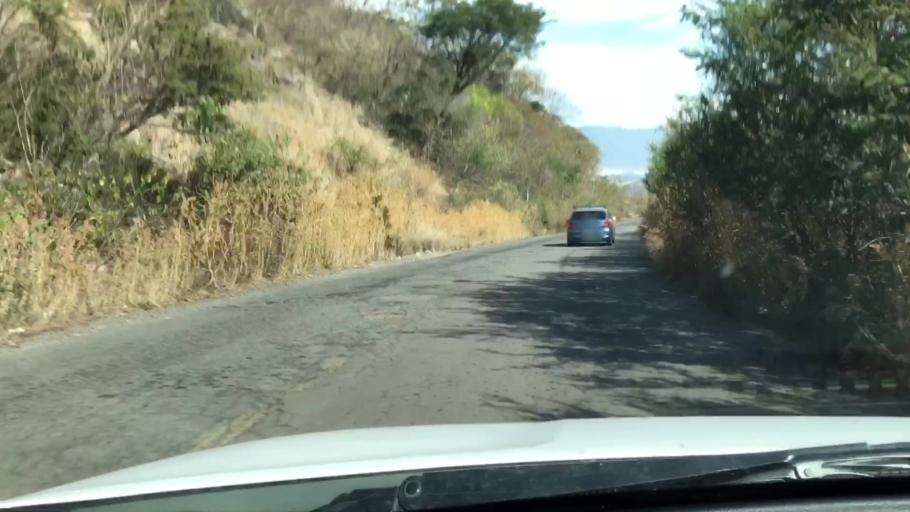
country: MX
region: Jalisco
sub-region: Zacoalco de Torres
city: Barranca de Otates (Barranca de Otatan)
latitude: 20.2438
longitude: -103.6819
